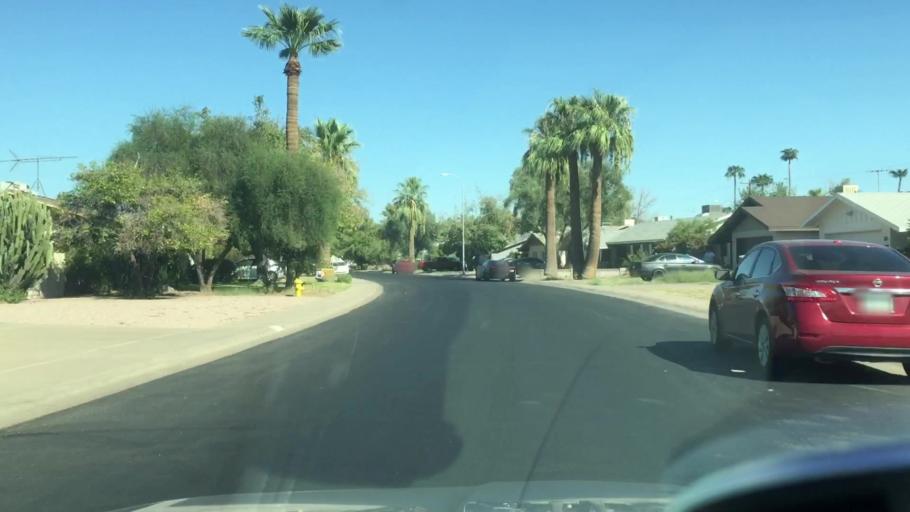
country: US
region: Arizona
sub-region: Maricopa County
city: Tempe Junction
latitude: 33.3951
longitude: -111.9373
